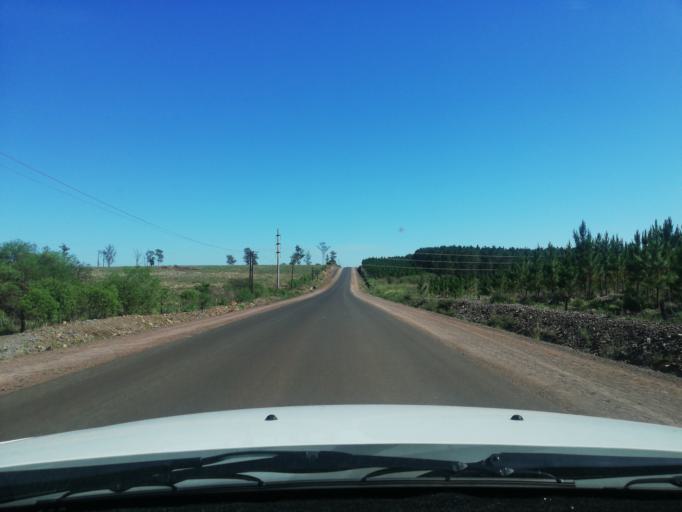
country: AR
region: Misiones
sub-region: Departamento de Candelaria
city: Candelaria
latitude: -27.5059
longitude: -55.7366
